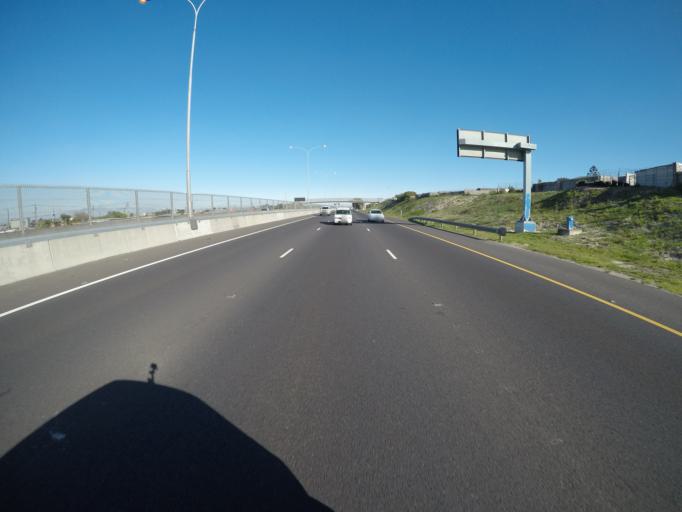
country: ZA
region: Western Cape
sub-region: City of Cape Town
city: Kraaifontein
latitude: -33.9658
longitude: 18.6550
